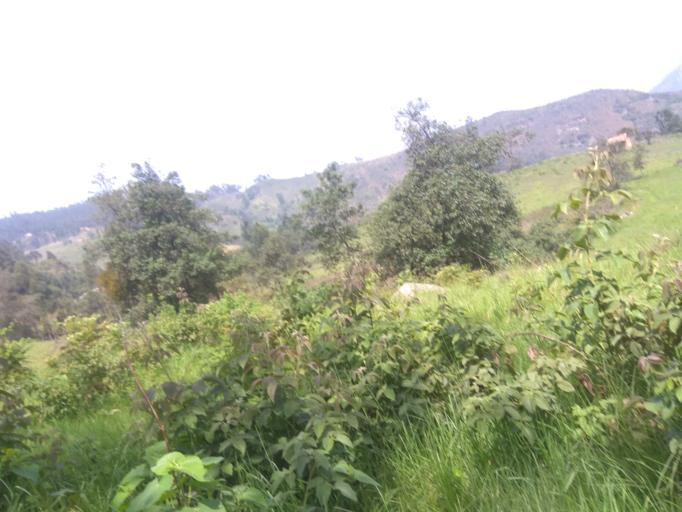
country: CO
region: Boyaca
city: Socha Viejo
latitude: 5.9804
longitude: -72.7220
